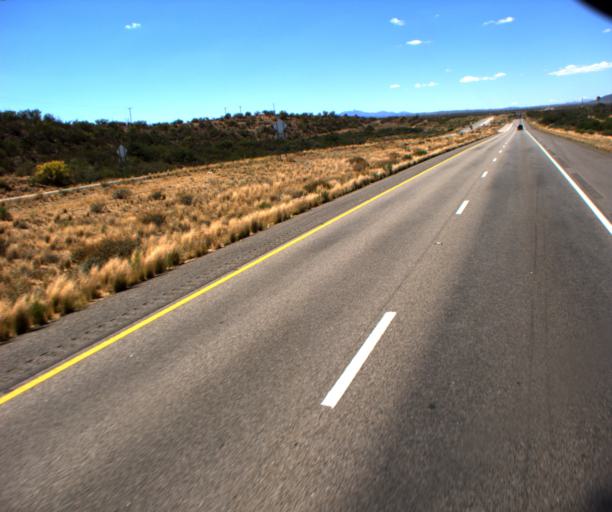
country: US
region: Arizona
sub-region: Yavapai County
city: Bagdad
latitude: 34.8275
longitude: -113.6290
